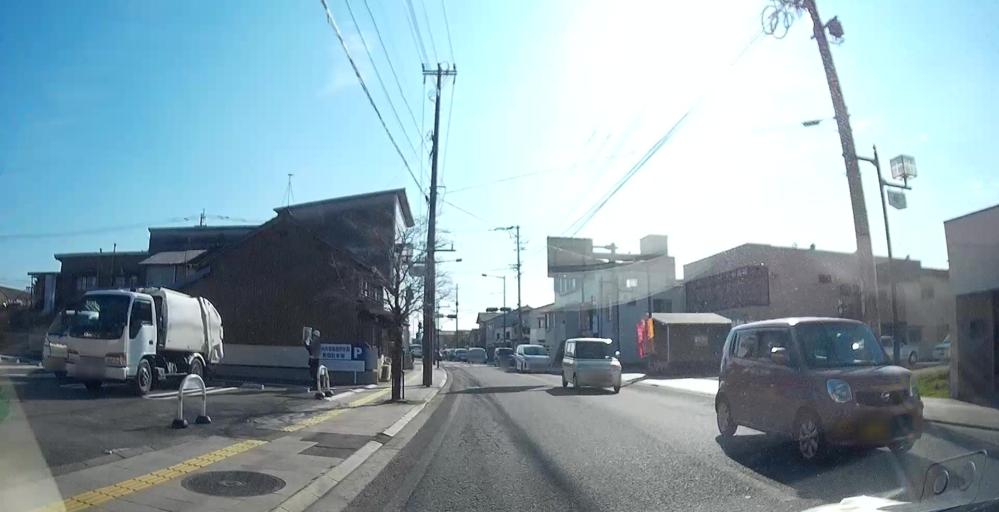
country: JP
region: Kumamoto
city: Uto
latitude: 32.7440
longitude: 130.6818
